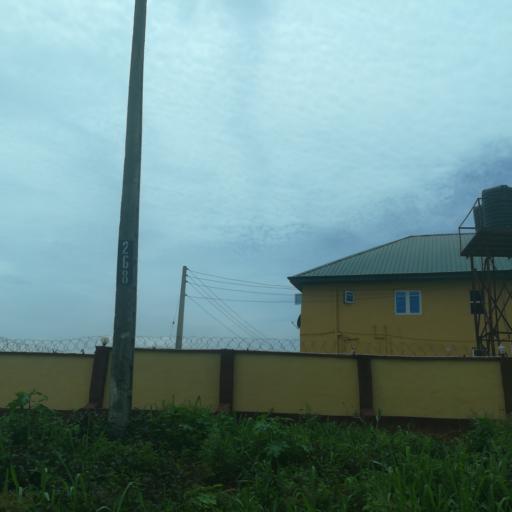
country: NG
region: Lagos
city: Ejirin
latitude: 6.6500
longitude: 3.7143
